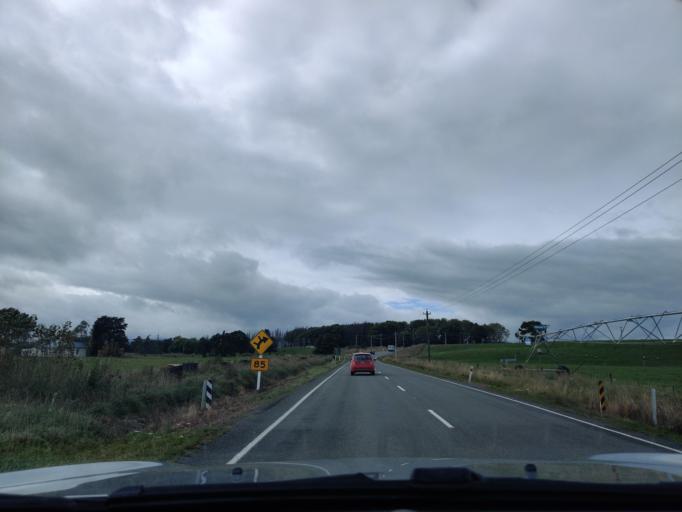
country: NZ
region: Canterbury
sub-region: Hurunui District
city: Amberley
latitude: -42.7148
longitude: 172.8641
